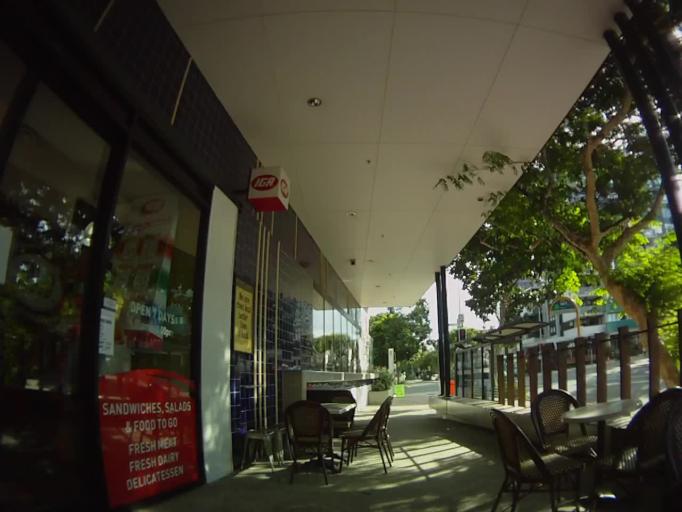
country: AU
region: Queensland
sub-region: Brisbane
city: South Brisbane
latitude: -27.4756
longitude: 153.0160
